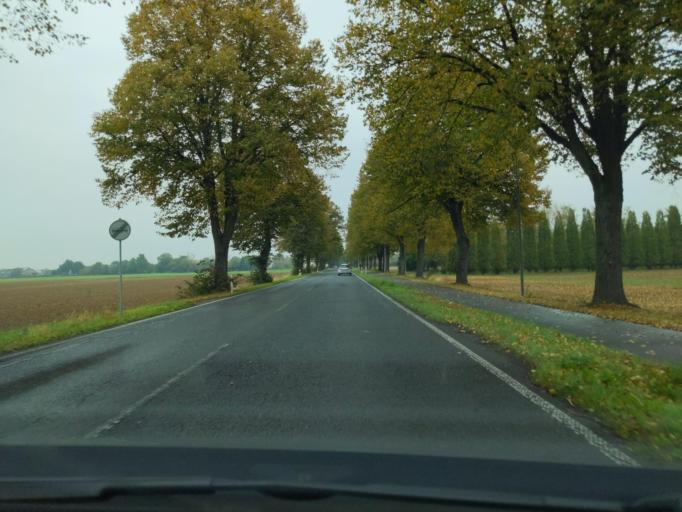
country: DE
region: North Rhine-Westphalia
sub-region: Regierungsbezirk Dusseldorf
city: Kaarst
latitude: 51.2115
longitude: 6.6091
